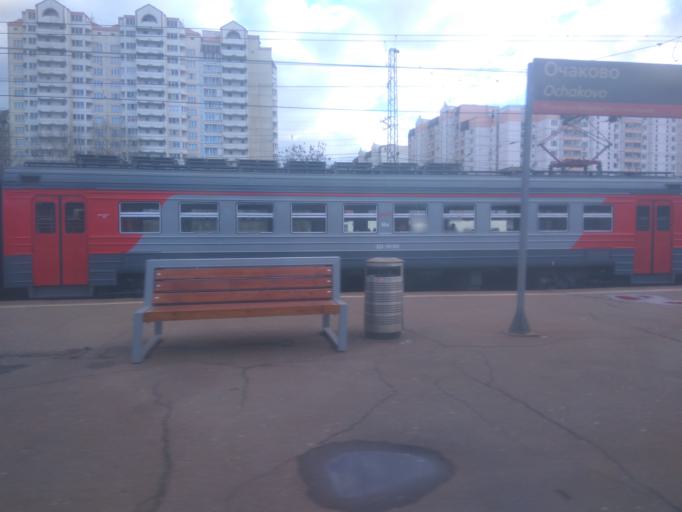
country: RU
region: Moscow
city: Ochakovo-Matveyevskoye
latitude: 55.6834
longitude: 37.4507
